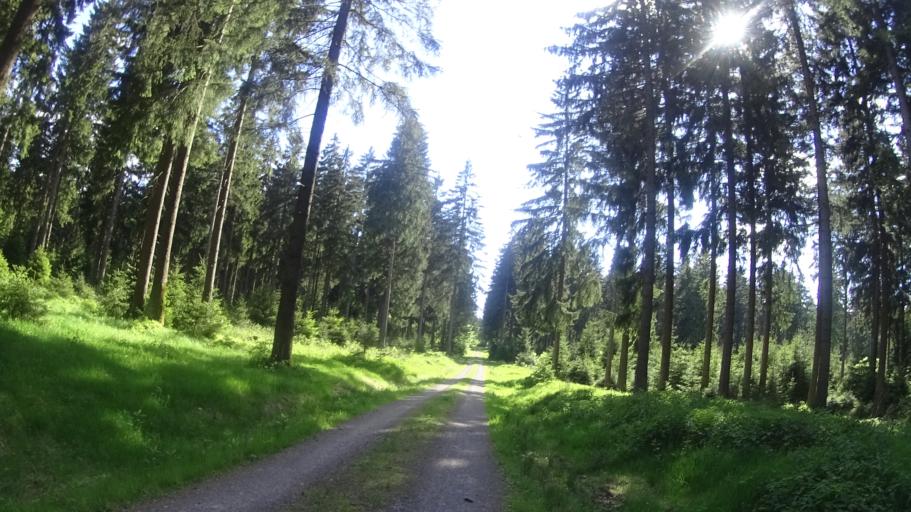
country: DE
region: Thuringia
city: Neustadt am Rennsteig
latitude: 50.5983
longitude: 10.9269
